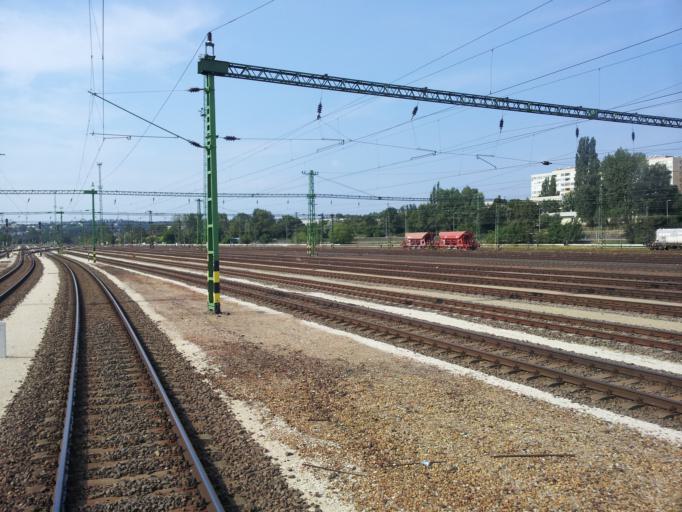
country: HU
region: Budapest
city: Budapest XI. keruelet
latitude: 47.4620
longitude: 19.0207
